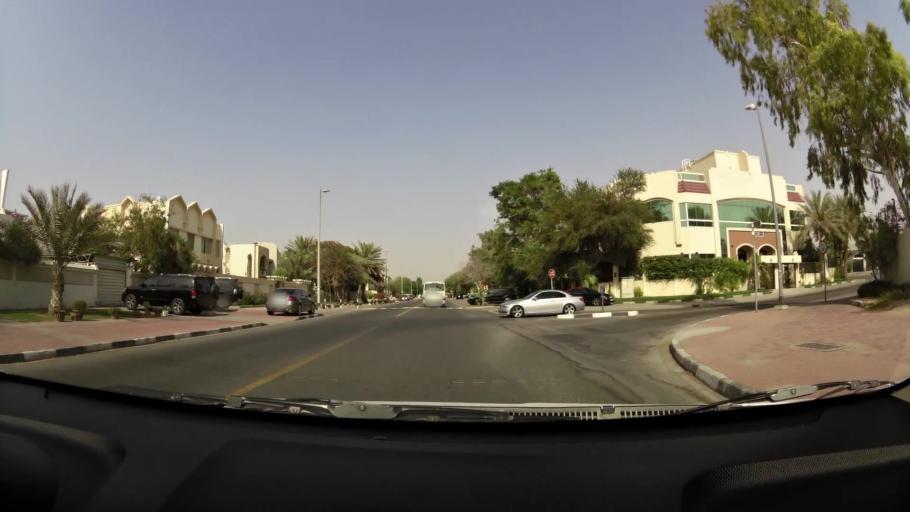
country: AE
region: Ash Shariqah
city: Sharjah
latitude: 25.2437
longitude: 55.3507
